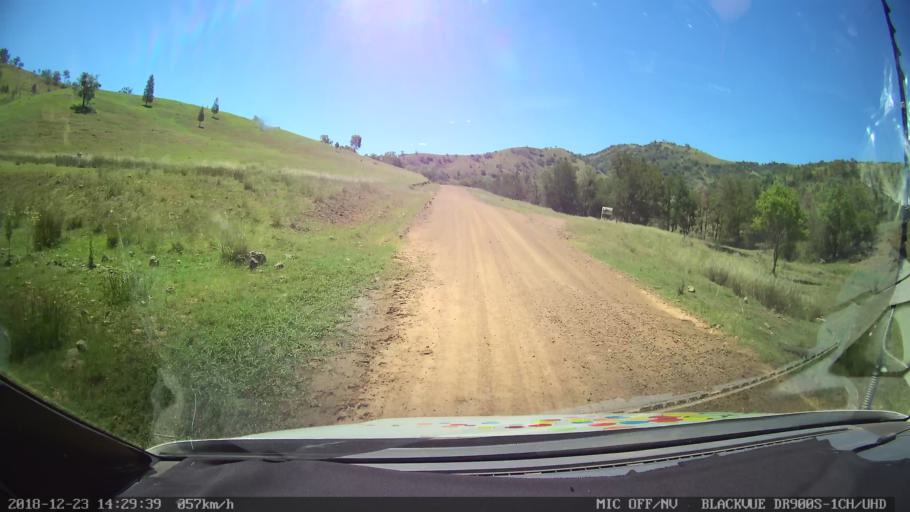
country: AU
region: New South Wales
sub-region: Tamworth Municipality
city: Manilla
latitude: -30.6073
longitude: 150.9370
